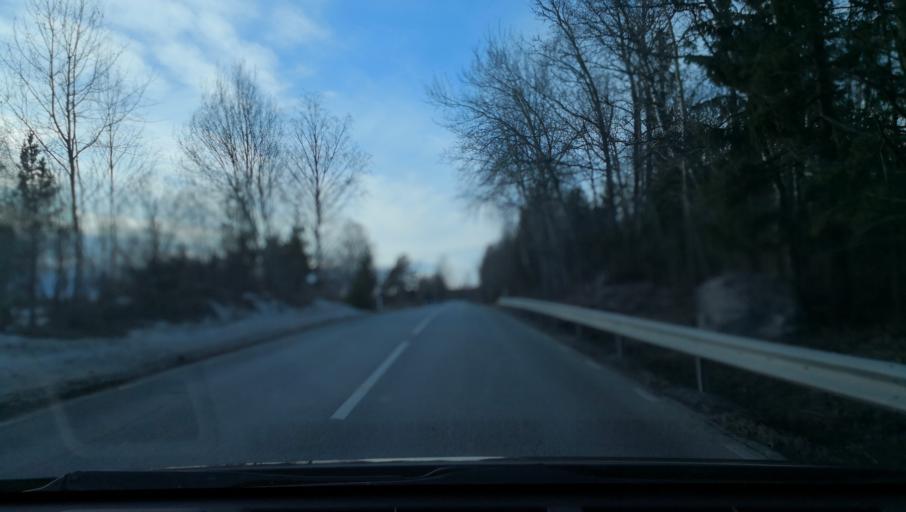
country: SE
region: Uppsala
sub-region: Osthammars Kommun
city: Gimo
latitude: 60.3366
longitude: 18.2220
